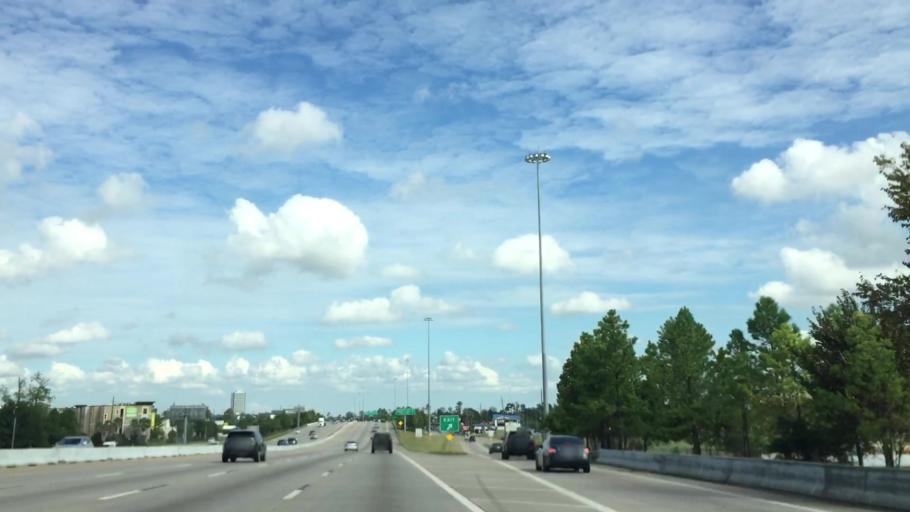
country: US
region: Texas
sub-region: Harris County
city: Oak Cliff Place
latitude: 29.9757
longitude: -95.5645
